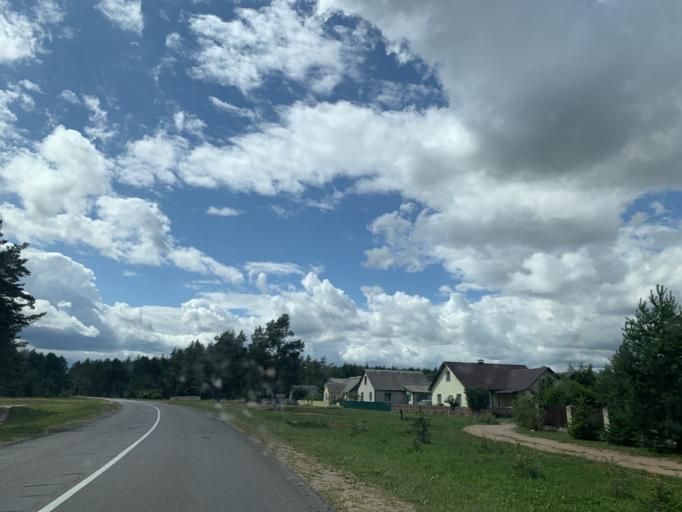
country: BY
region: Minsk
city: Rakaw
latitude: 53.9867
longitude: 26.9465
